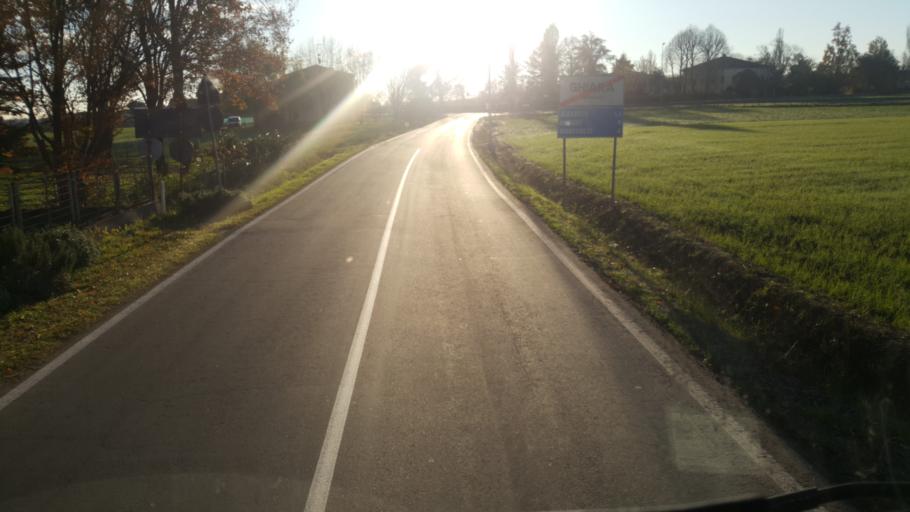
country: IT
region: Emilia-Romagna
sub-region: Provincia di Parma
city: Fontanellato
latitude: 44.8769
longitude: 10.1931
